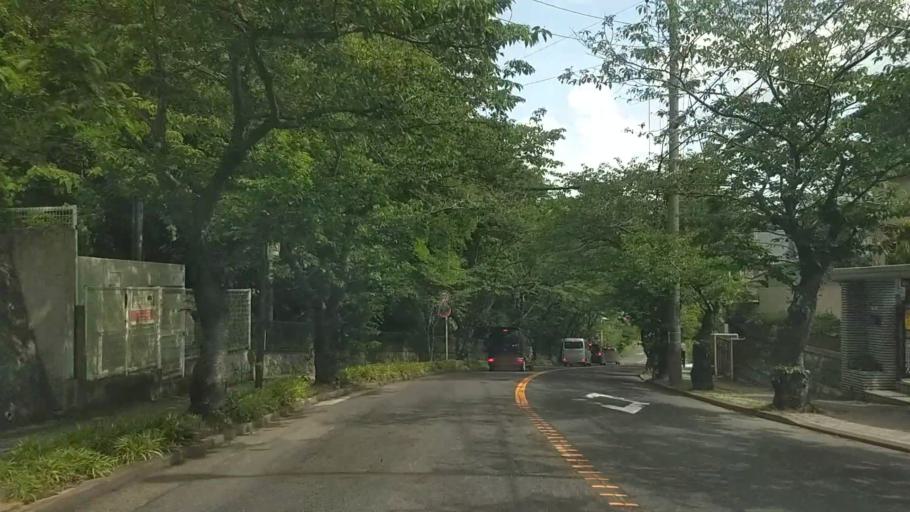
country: JP
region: Kanagawa
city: Zushi
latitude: 35.3167
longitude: 139.5767
